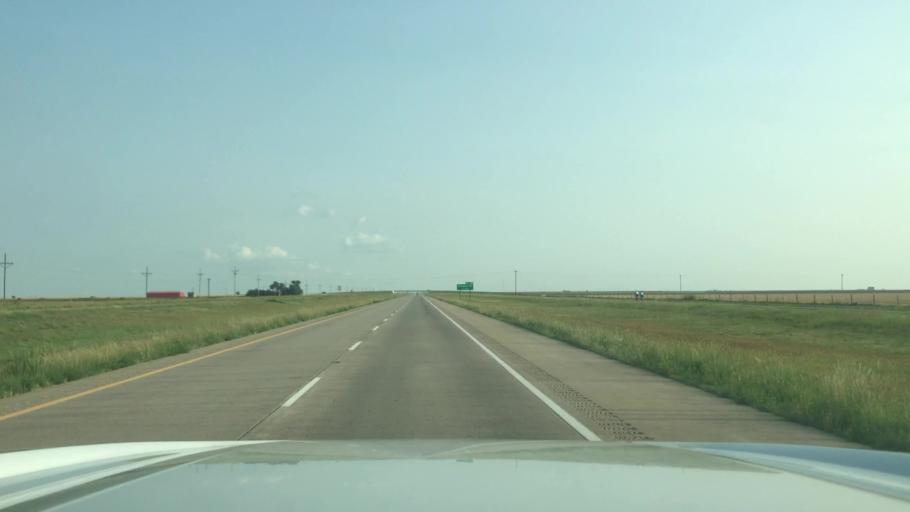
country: US
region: Texas
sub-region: Randall County
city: Canyon
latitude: 34.9008
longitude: -101.8487
